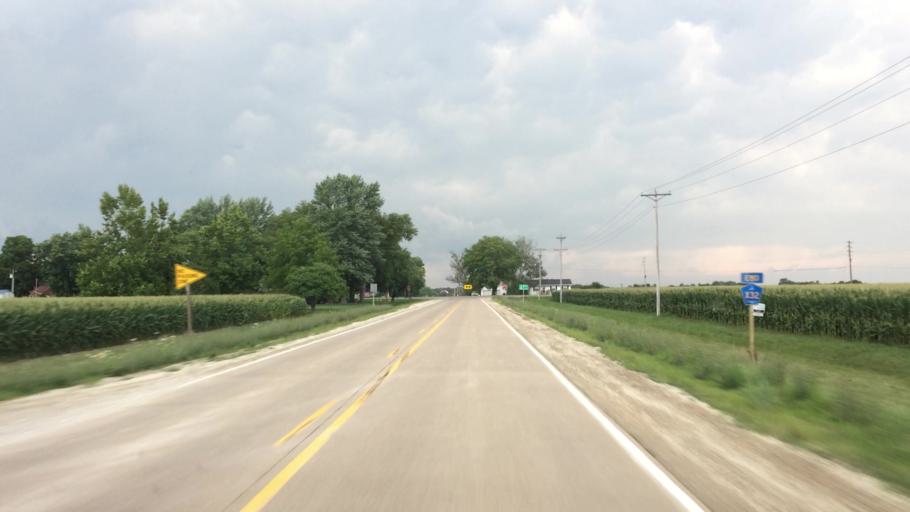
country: US
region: Iowa
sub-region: Lee County
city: Fort Madison
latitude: 40.7398
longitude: -91.3282
